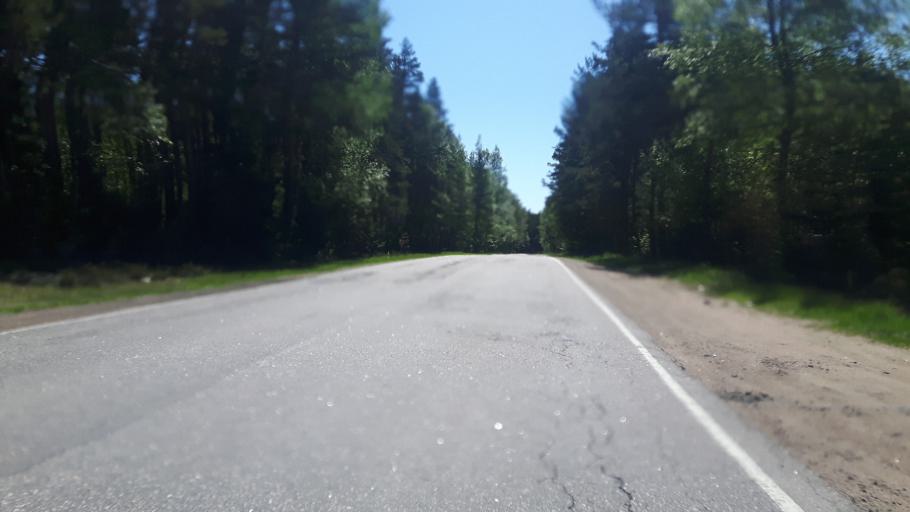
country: RU
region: Leningrad
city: Glebychevo
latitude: 60.3392
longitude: 28.8229
